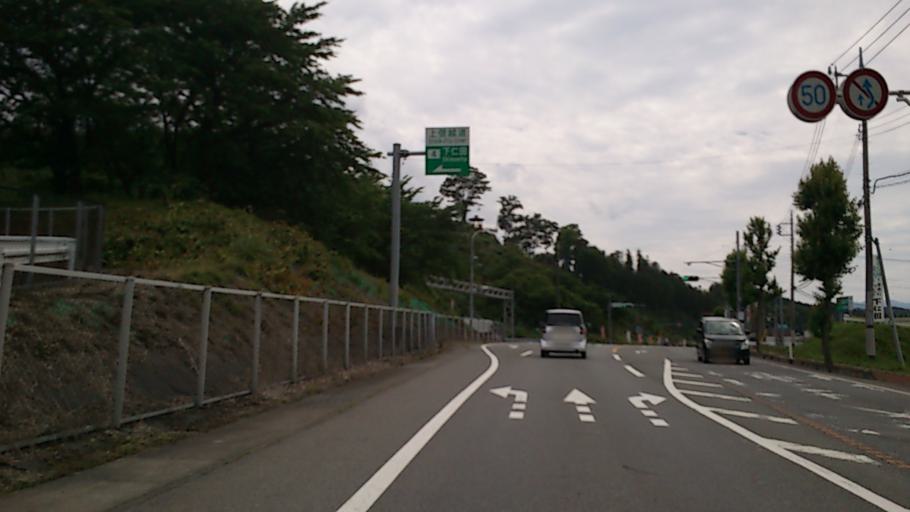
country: JP
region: Gunma
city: Tomioka
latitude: 36.2333
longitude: 138.8219
